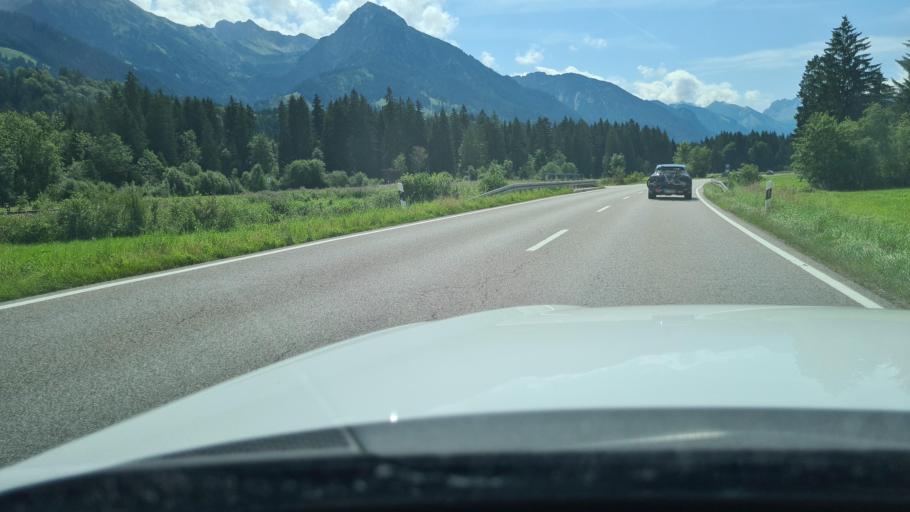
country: DE
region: Bavaria
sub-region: Swabia
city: Obermaiselstein
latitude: 47.4542
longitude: 10.2714
